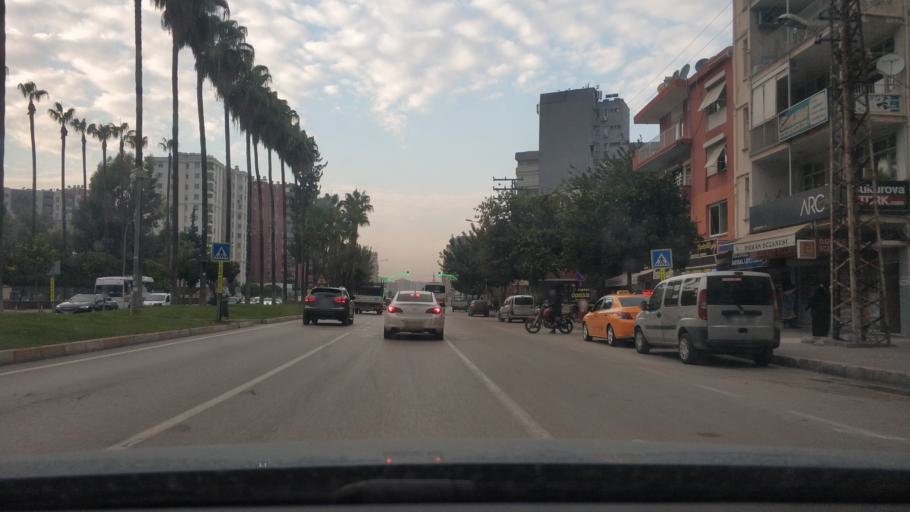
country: TR
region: Adana
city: Adana
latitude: 37.0007
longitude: 35.3151
